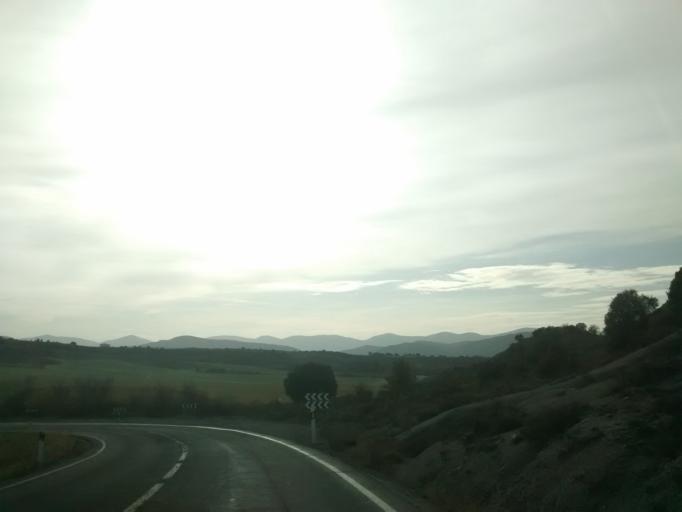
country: ES
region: Aragon
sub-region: Provincia de Zaragoza
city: Mianos
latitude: 42.6078
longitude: -0.8726
